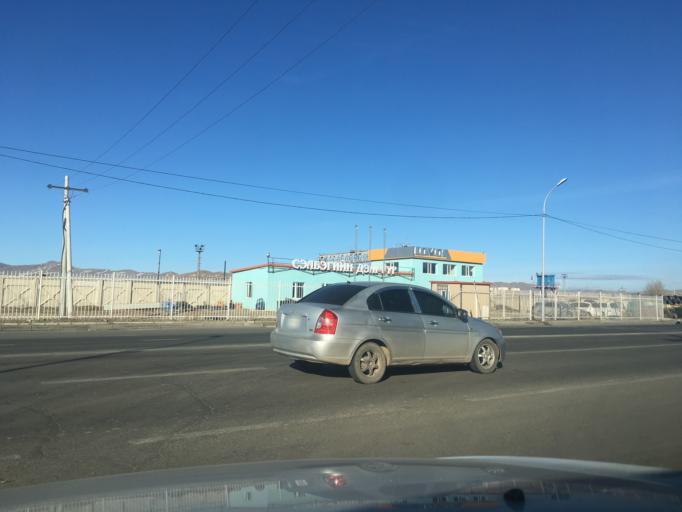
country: MN
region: Ulaanbaatar
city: Ulaanbaatar
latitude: 47.9054
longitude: 106.7646
